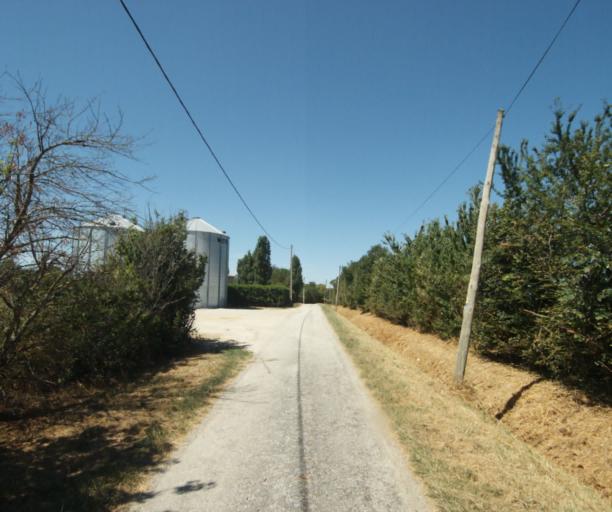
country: FR
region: Midi-Pyrenees
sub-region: Departement de la Haute-Garonne
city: Saint-Felix-Lauragais
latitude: 43.4710
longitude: 1.9418
